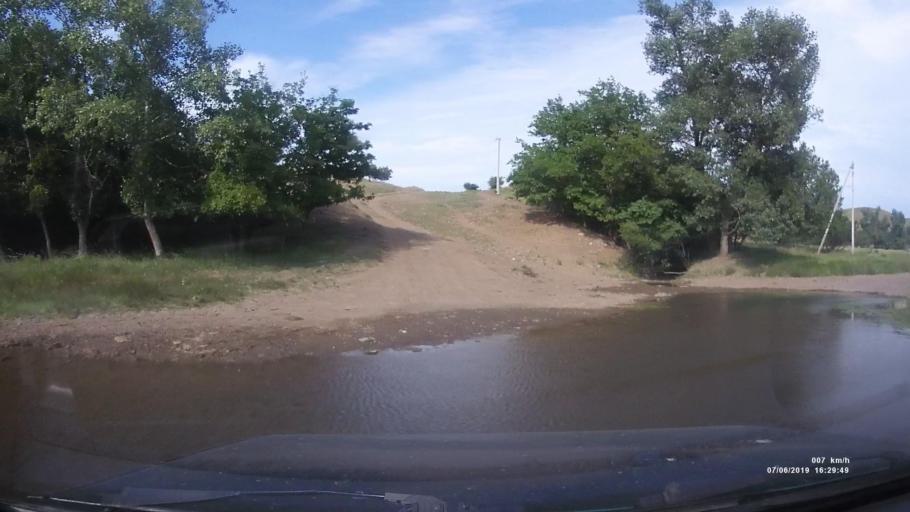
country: RU
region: Rostov
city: Staraya Stanitsa
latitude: 48.2550
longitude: 40.3218
